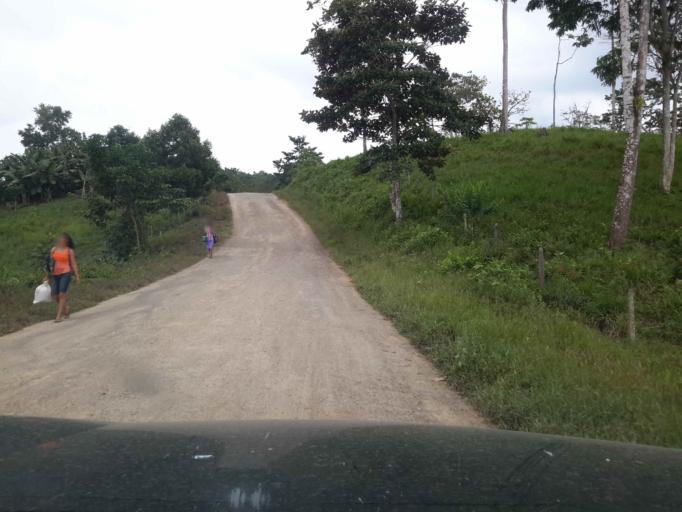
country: CR
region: Alajuela
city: Los Chiles
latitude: 11.1107
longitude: -84.5871
